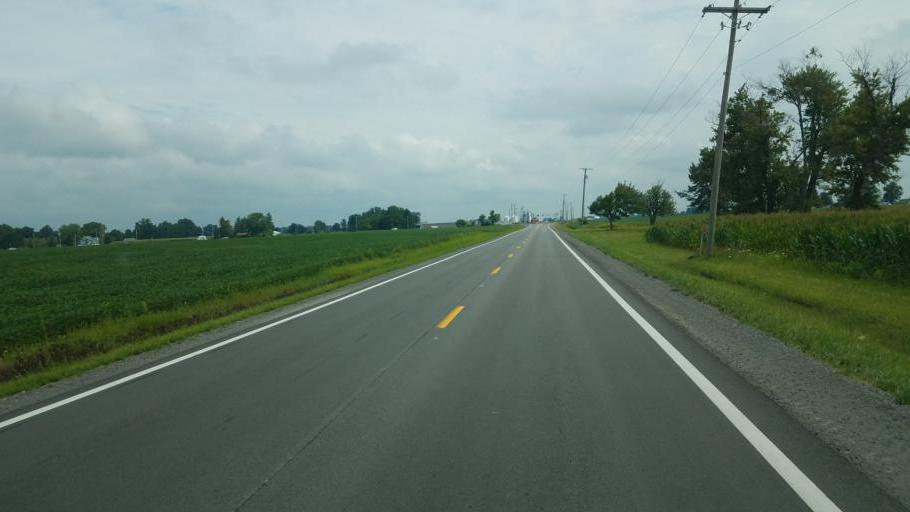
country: US
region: Ohio
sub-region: Marion County
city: Marion
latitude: 40.5774
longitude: -83.0416
